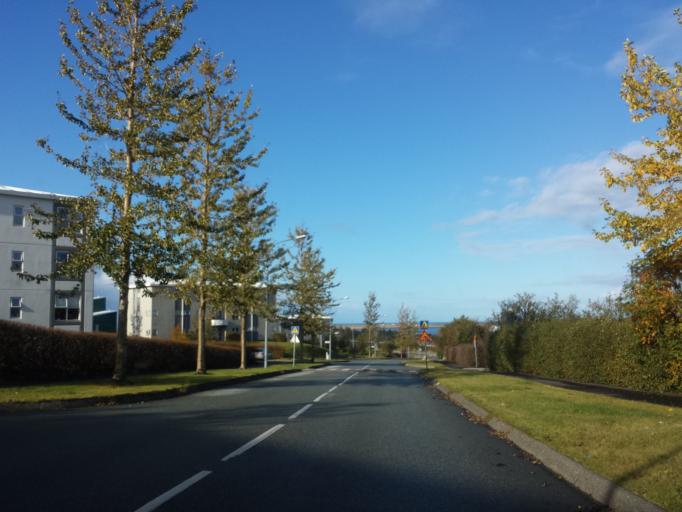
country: IS
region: Capital Region
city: Kopavogur
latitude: 64.0993
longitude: -21.9001
